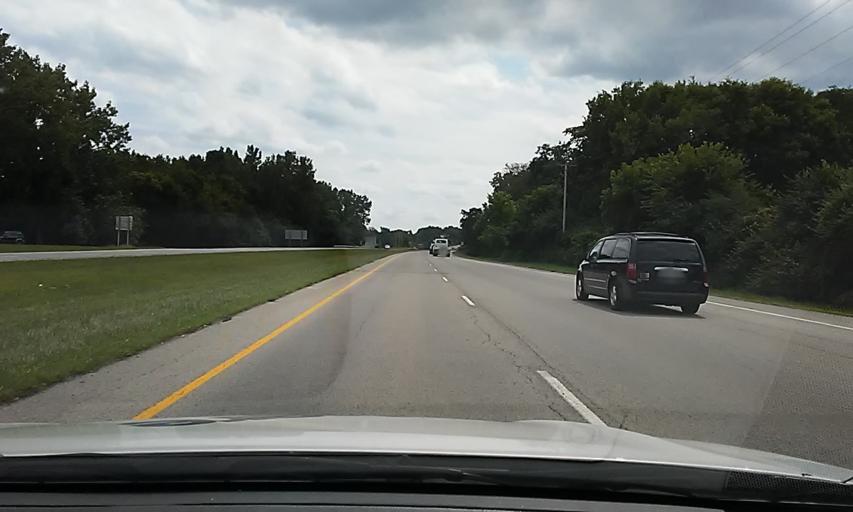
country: US
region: Ohio
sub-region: Greene County
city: Wright-Patterson AFB
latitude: 39.8427
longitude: -84.0593
